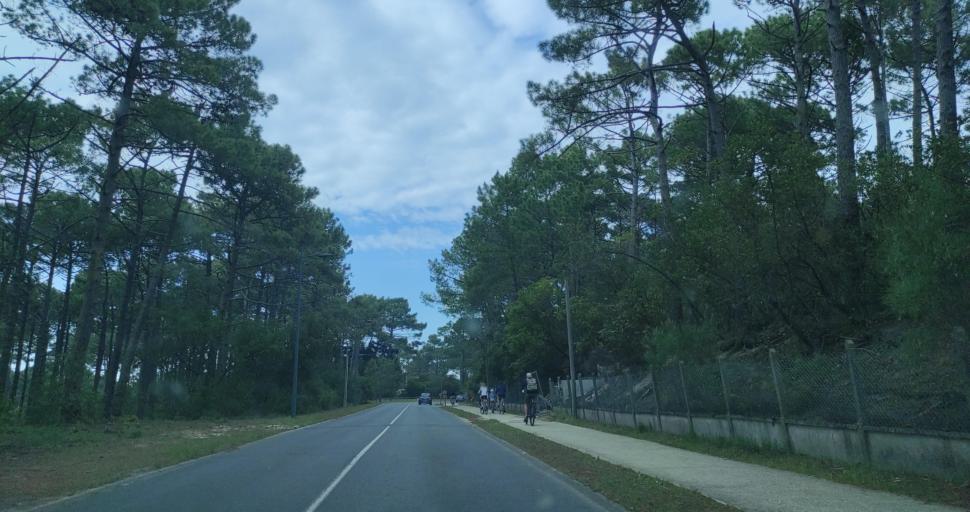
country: FR
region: Aquitaine
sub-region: Departement de la Gironde
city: Arcachon
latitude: 44.6814
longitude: -1.2393
